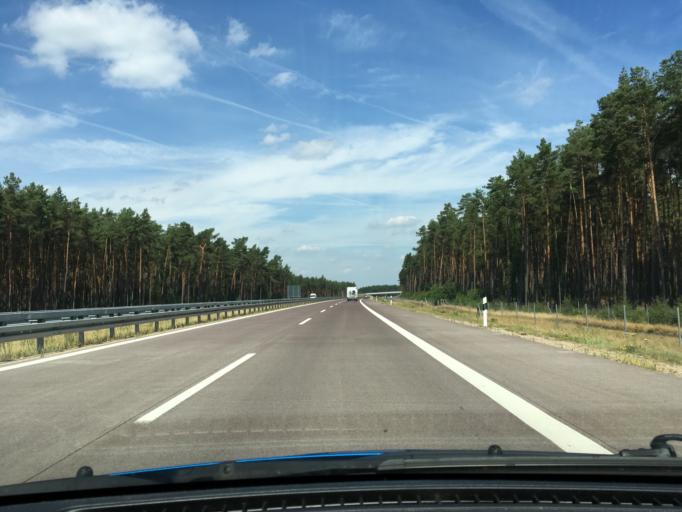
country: DE
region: Mecklenburg-Vorpommern
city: Ludwigslust
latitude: 53.3509
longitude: 11.5169
